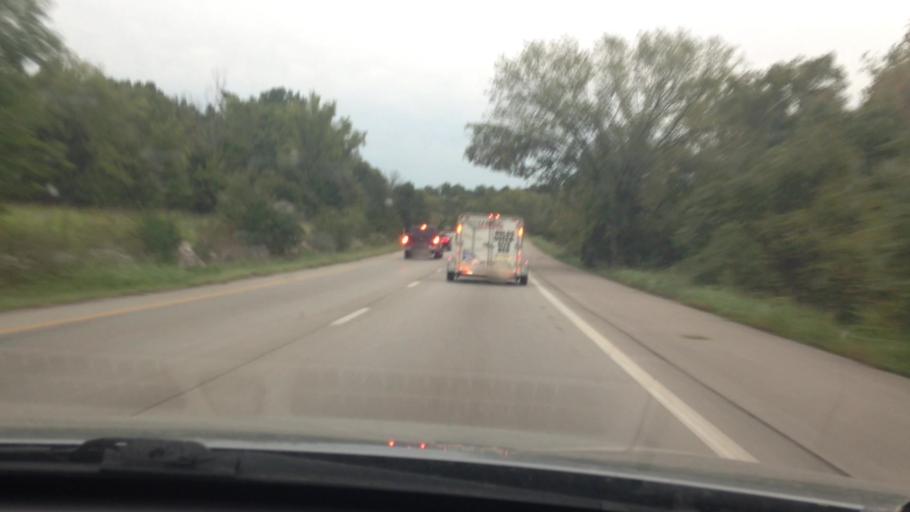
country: US
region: Missouri
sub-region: Jackson County
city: Raytown
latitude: 38.9701
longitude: -94.4408
